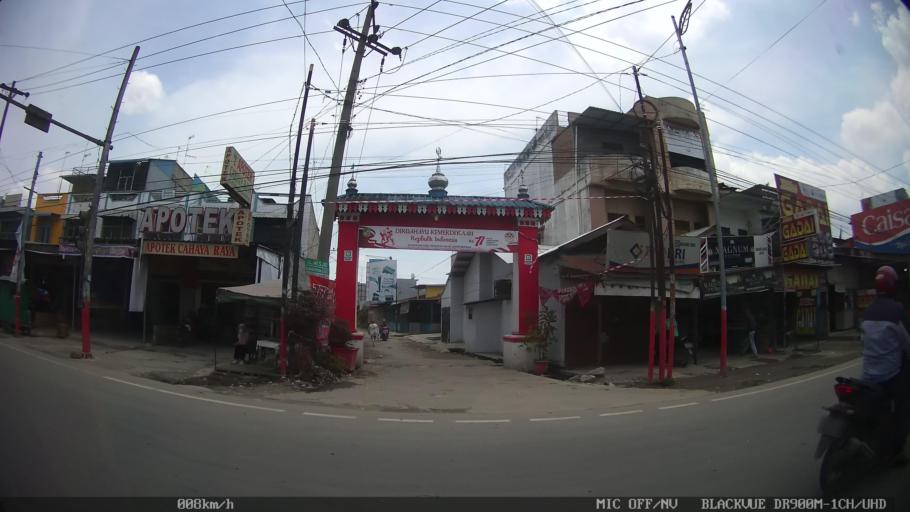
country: ID
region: North Sumatra
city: Labuhan Deli
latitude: 3.7107
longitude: 98.6607
